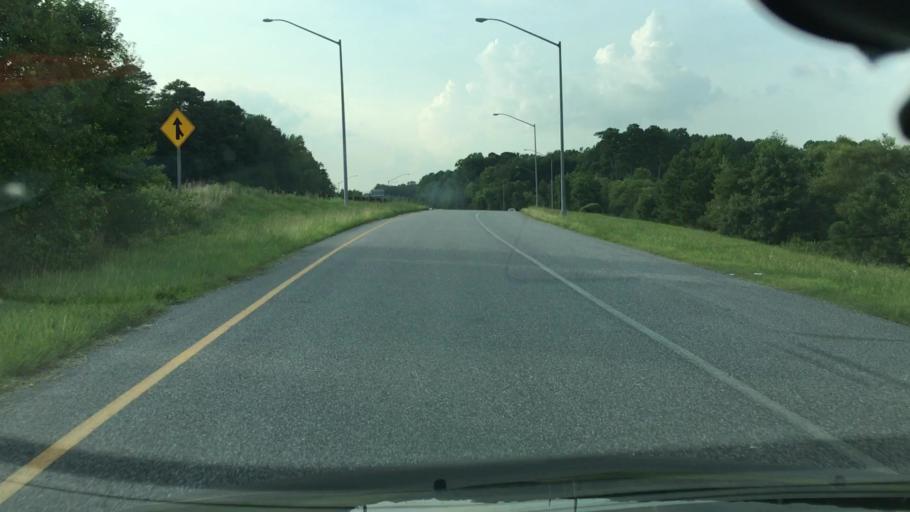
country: US
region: Maryland
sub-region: Worcester County
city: Ocean Pines
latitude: 38.3920
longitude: -75.2033
